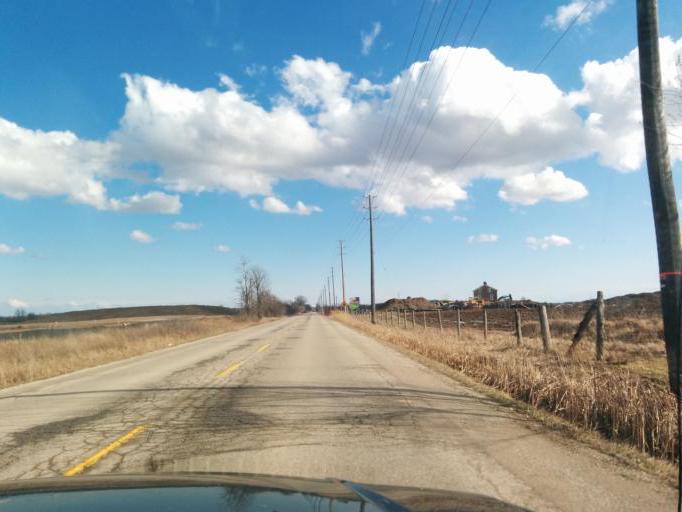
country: CA
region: Ontario
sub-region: Halton
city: Milton
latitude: 43.4798
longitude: -79.8493
